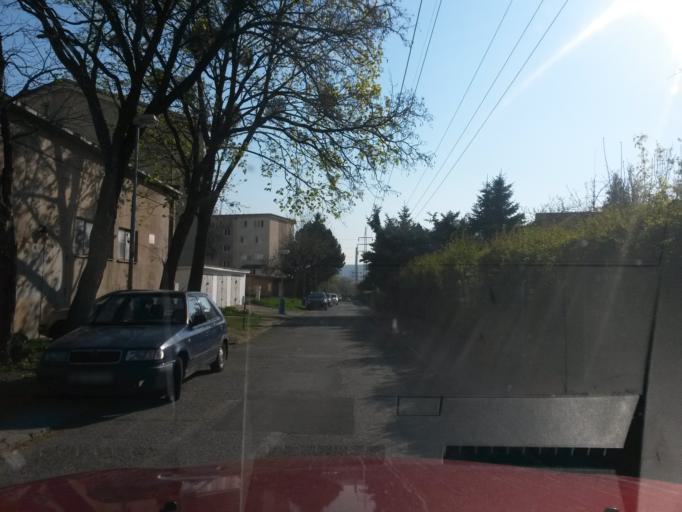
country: SK
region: Kosicky
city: Kosice
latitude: 48.7465
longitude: 21.2444
